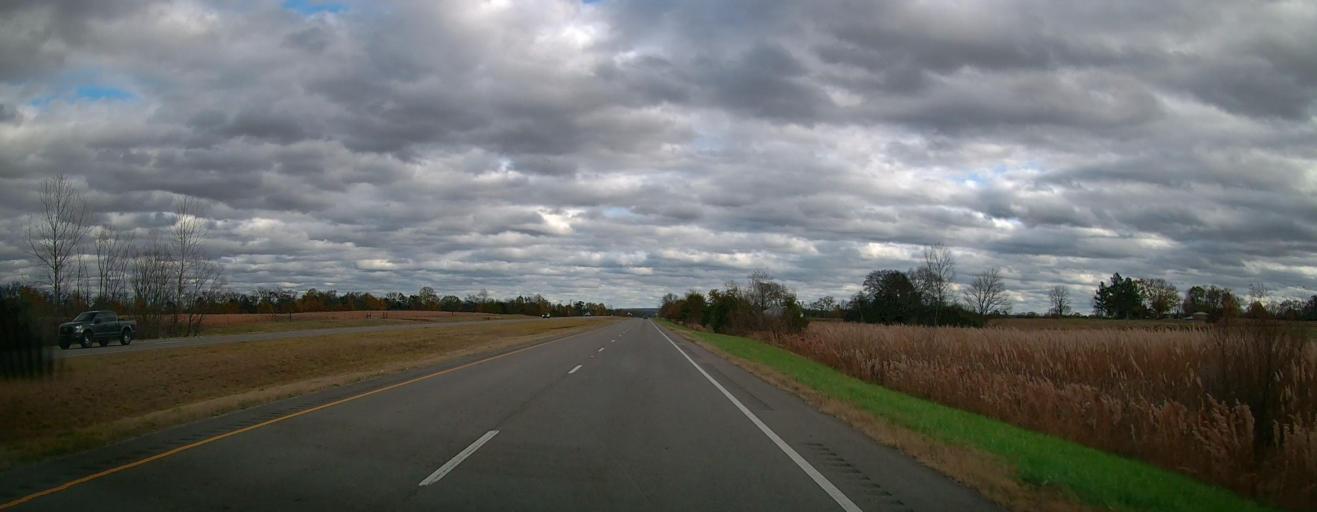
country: US
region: Alabama
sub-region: Morgan County
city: Danville
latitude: 34.3825
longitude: -87.0990
